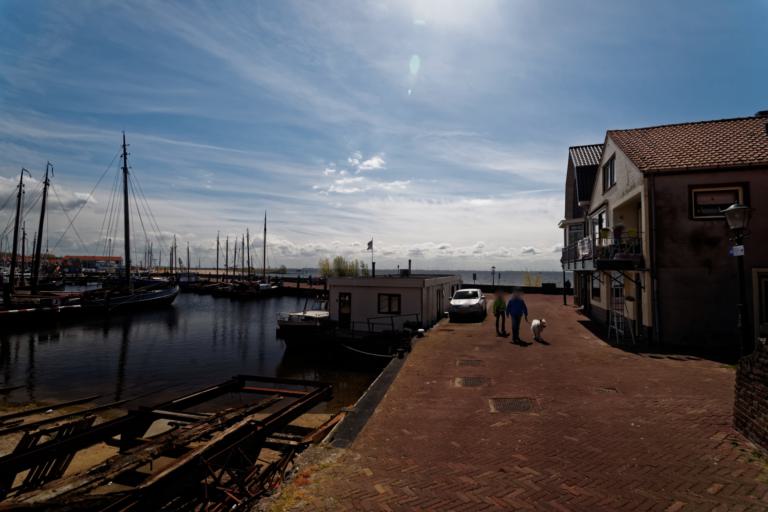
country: NL
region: Flevoland
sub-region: Gemeente Urk
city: Urk
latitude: 52.6610
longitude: 5.5932
